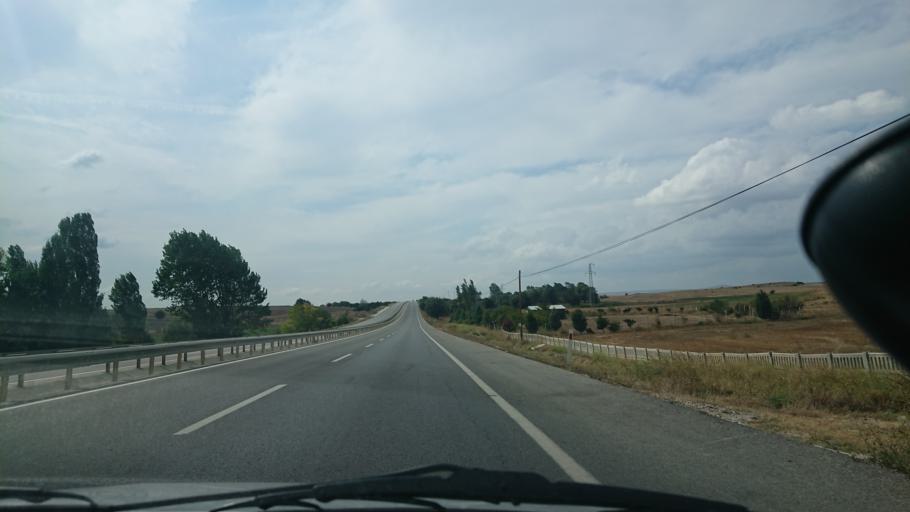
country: TR
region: Eskisehir
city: Eskisehir
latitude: 39.7252
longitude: 30.3311
